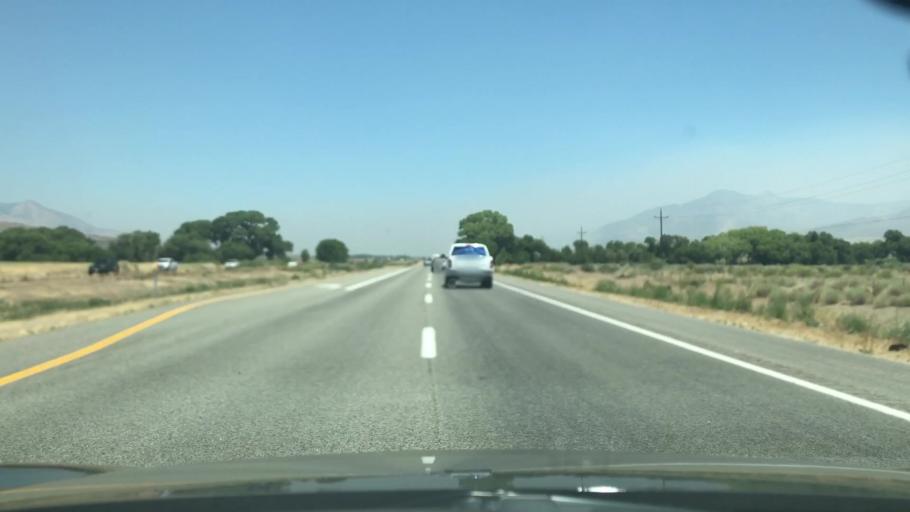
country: US
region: California
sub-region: Inyo County
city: Big Pine
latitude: 37.0773
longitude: -118.2436
